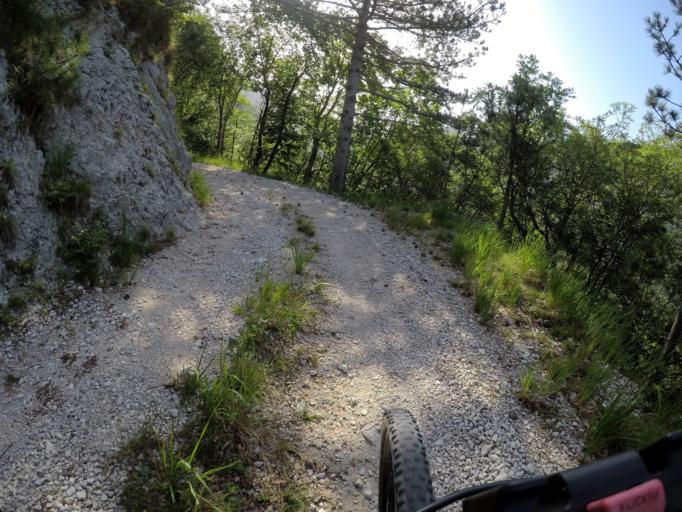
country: IT
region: Friuli Venezia Giulia
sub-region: Provincia di Udine
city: Resiutta
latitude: 46.3255
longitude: 13.2208
